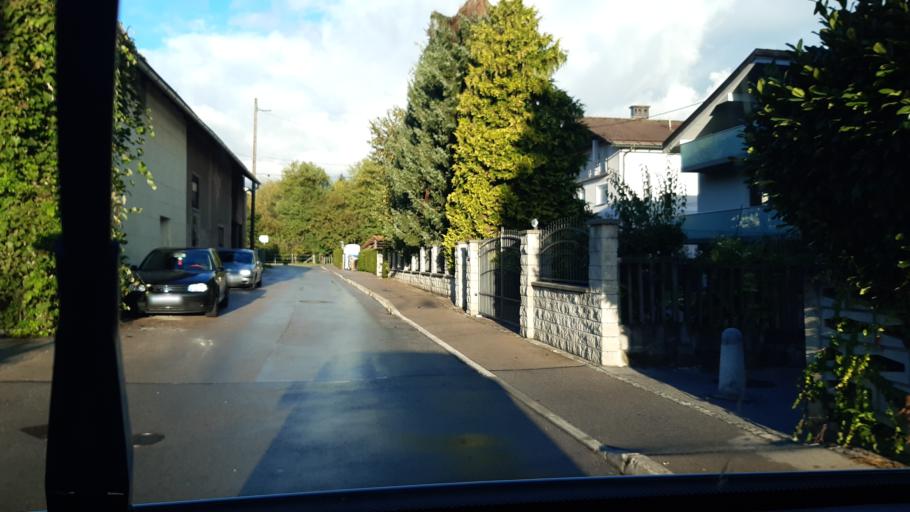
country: SI
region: Ljubljana
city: Ljubljana
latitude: 46.0508
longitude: 14.5417
